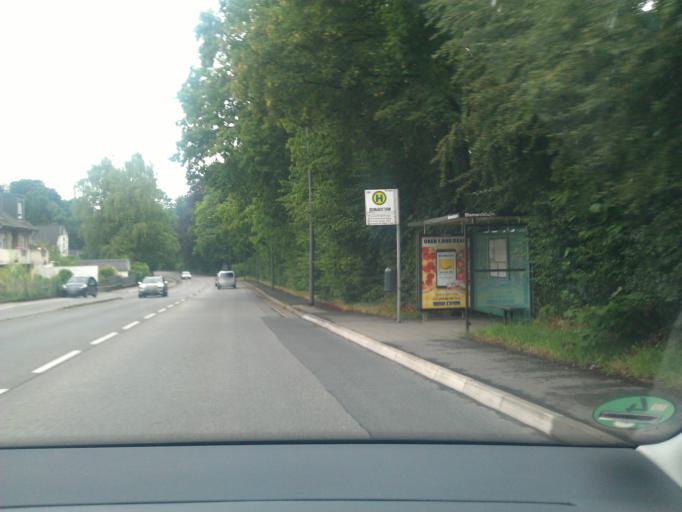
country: DE
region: North Rhine-Westphalia
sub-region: Regierungsbezirk Koln
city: Aachen
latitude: 50.7481
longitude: 6.1028
